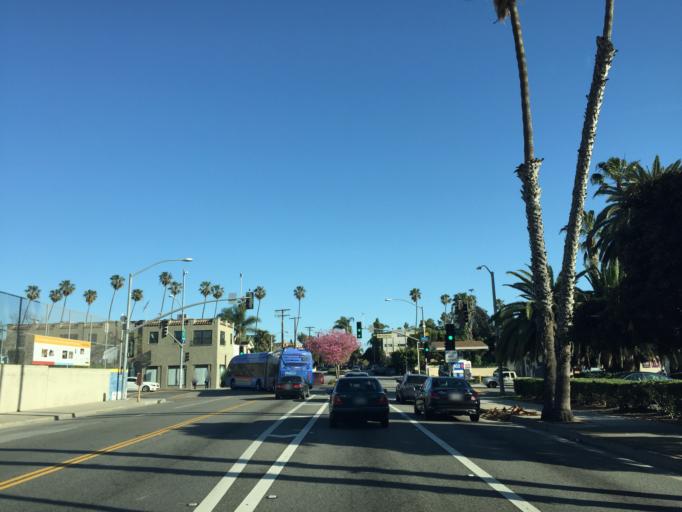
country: US
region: California
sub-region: Los Angeles County
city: Santa Monica
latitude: 34.0100
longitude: -118.4878
